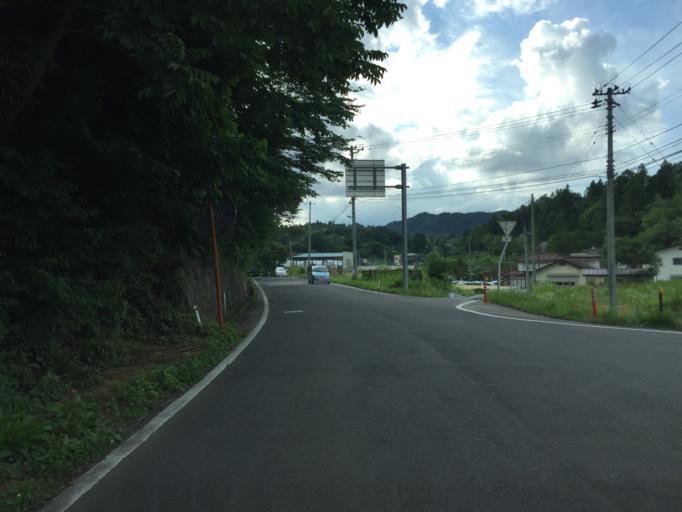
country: JP
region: Fukushima
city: Fukushima-shi
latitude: 37.6830
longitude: 140.5710
